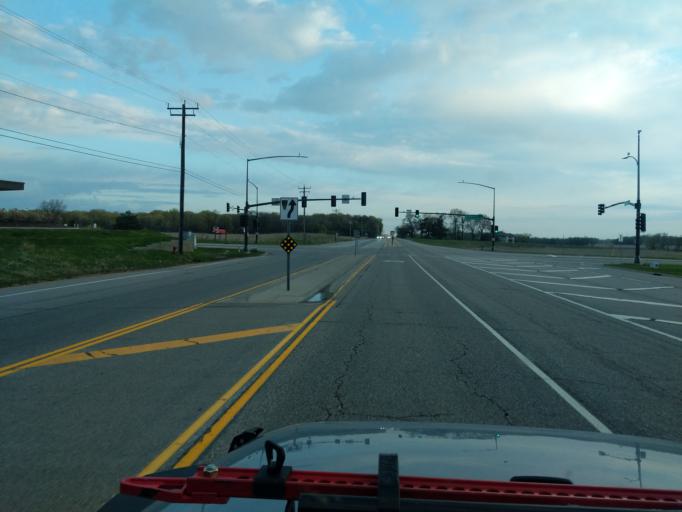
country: US
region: Minnesota
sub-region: Hennepin County
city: Rogers
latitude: 45.1822
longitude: -93.5233
